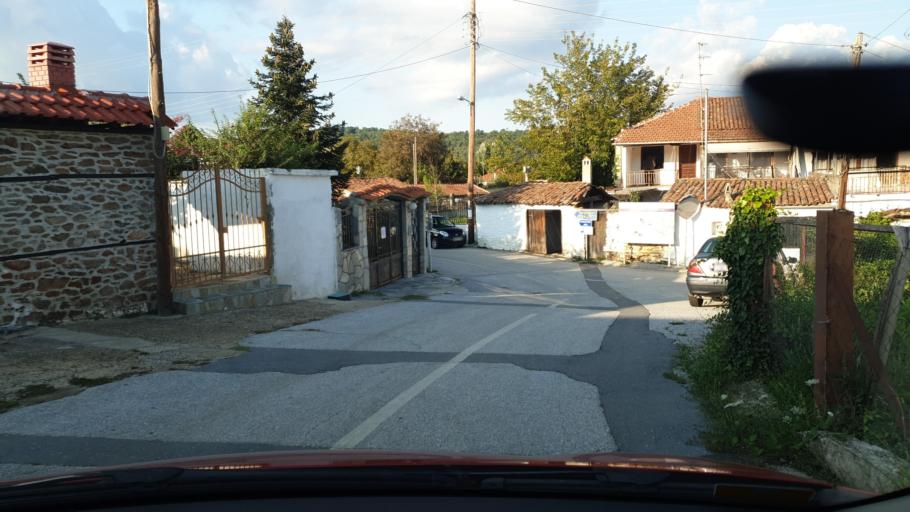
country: GR
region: Central Macedonia
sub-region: Nomos Chalkidikis
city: Galatista
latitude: 40.5172
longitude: 23.2840
